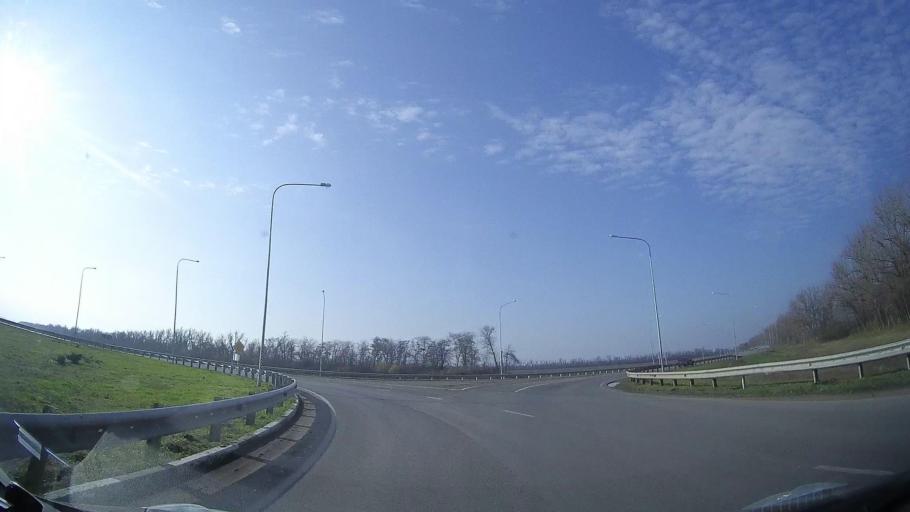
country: RU
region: Rostov
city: Tselina
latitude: 46.5329
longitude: 40.9843
